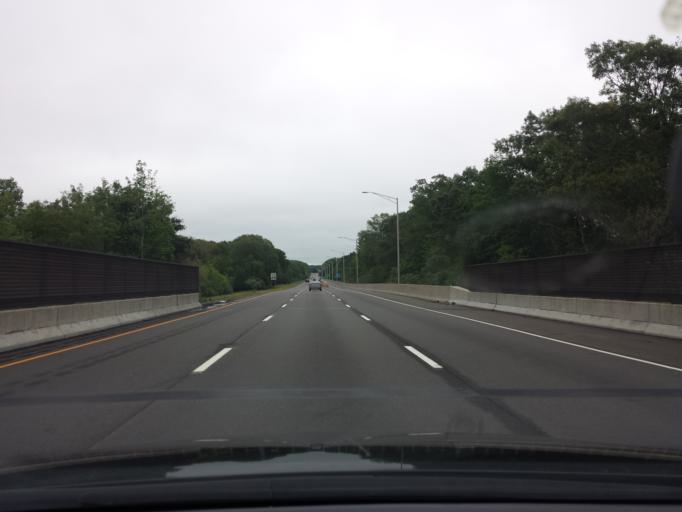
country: US
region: Connecticut
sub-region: New London County
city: Long Hill
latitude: 41.3598
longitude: -72.0404
